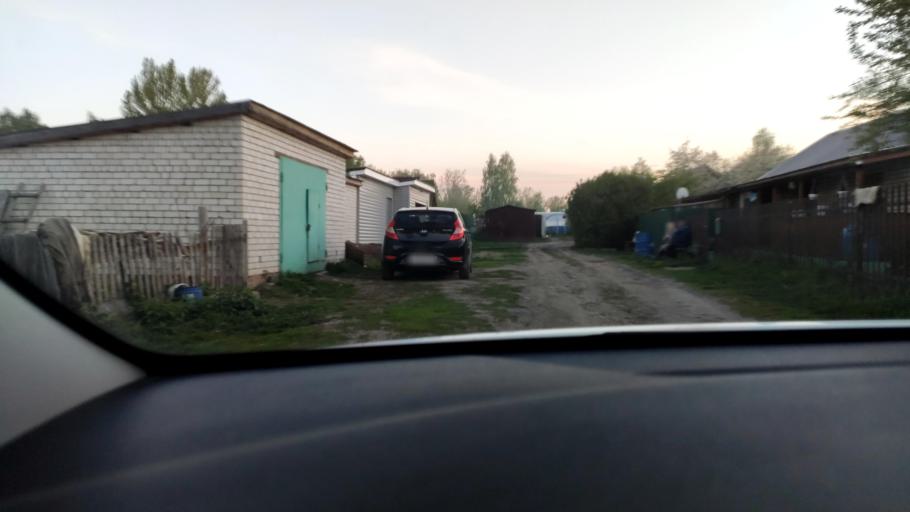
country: RU
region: Tatarstan
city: Stolbishchi
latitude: 55.7381
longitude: 49.2717
